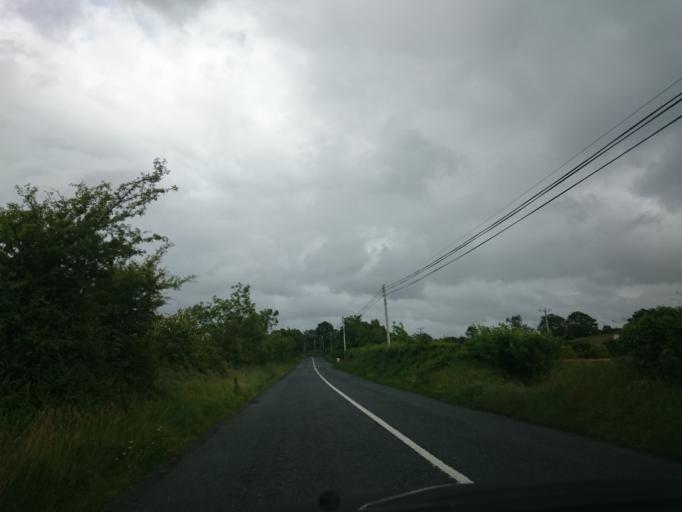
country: IE
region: Connaught
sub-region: Maigh Eo
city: Crossmolina
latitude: 54.2273
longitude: -9.2579
